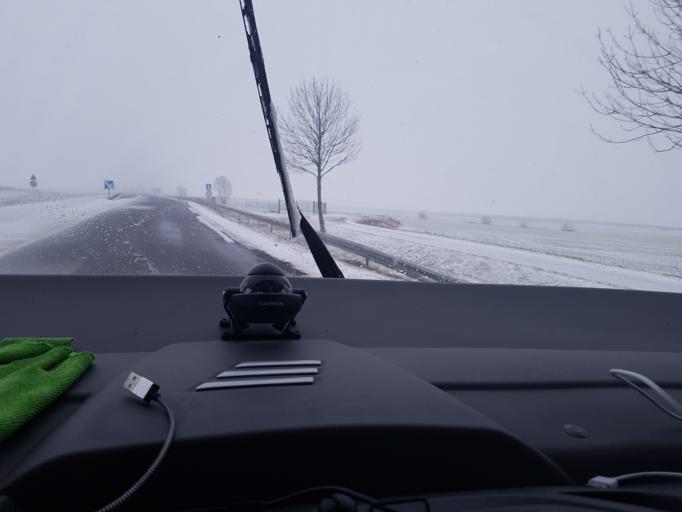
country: FR
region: Lorraine
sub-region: Departement de la Moselle
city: Chateau-Salins
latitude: 48.8585
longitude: 6.4415
